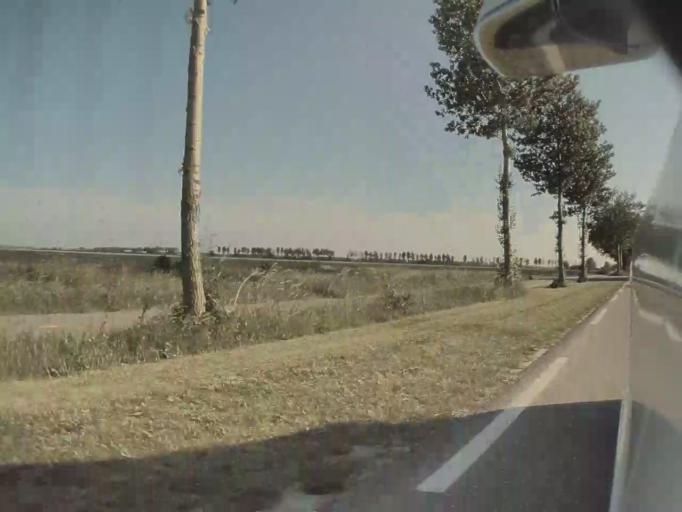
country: NL
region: Zeeland
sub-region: Gemeente Goes
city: Goes
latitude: 51.5907
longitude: 3.8334
